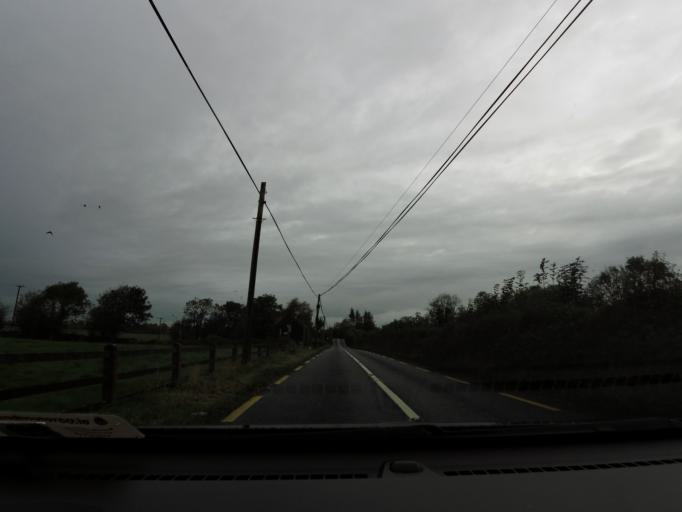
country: IE
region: Connaught
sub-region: County Galway
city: Tuam
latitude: 53.5437
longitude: -8.8100
